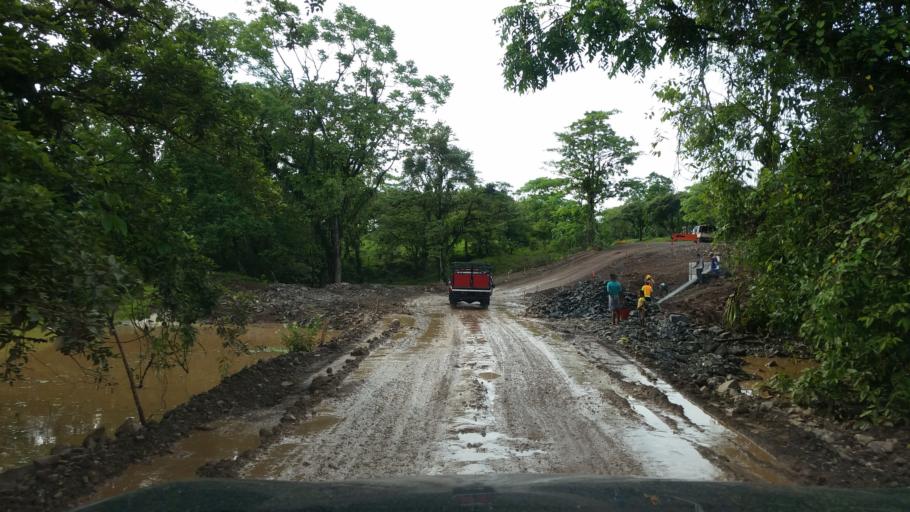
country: NI
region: Matagalpa
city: Rio Blanco
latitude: 13.0824
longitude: -85.0613
